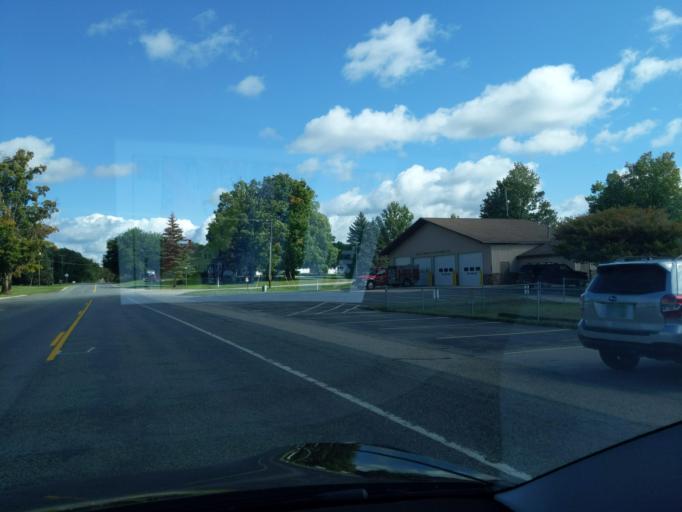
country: US
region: Michigan
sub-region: Antrim County
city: Elk Rapids
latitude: 44.9316
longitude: -85.3645
